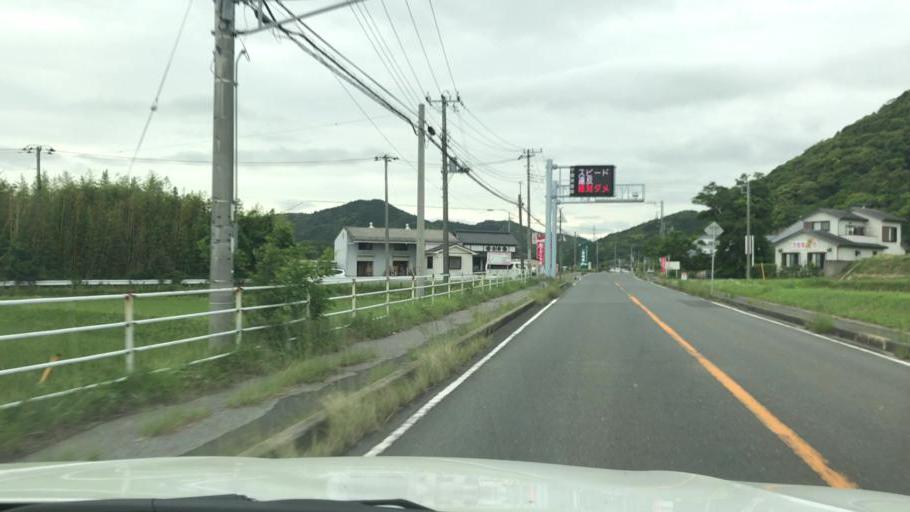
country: JP
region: Chiba
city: Kawaguchi
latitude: 35.1244
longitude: 140.0811
